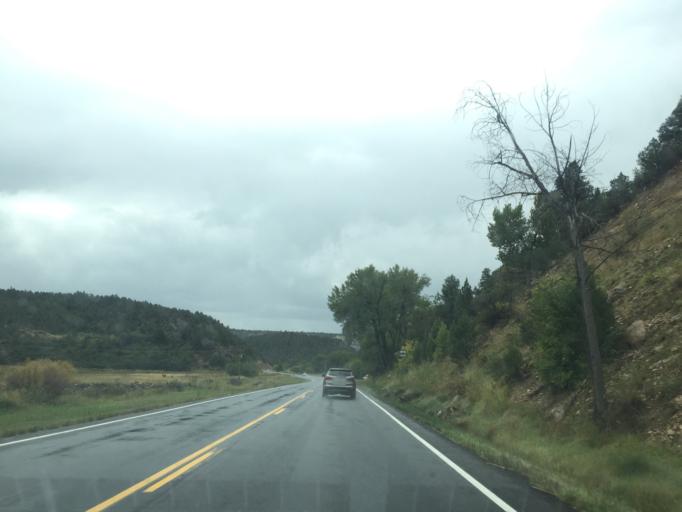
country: US
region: Utah
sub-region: Kane County
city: Kanab
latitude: 37.3374
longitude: -112.6042
